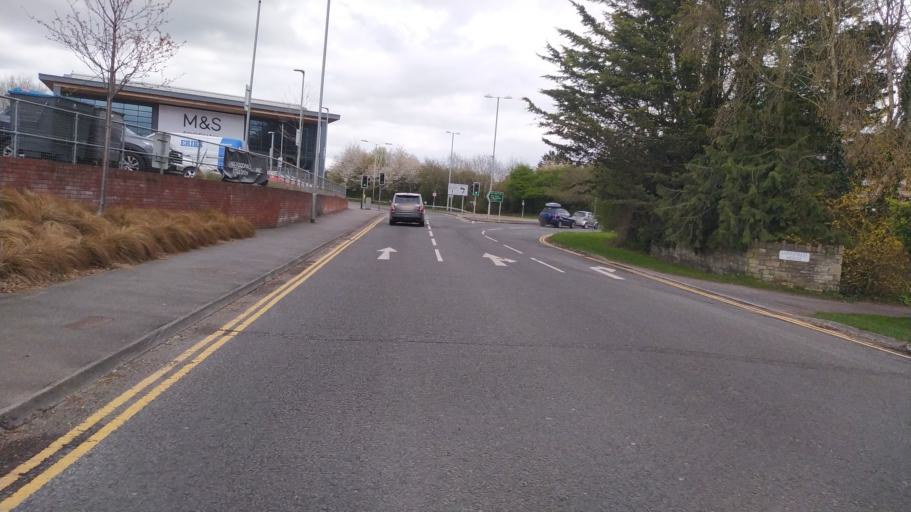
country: GB
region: England
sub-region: Wiltshire
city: Trowbridge
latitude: 51.3171
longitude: -2.2071
